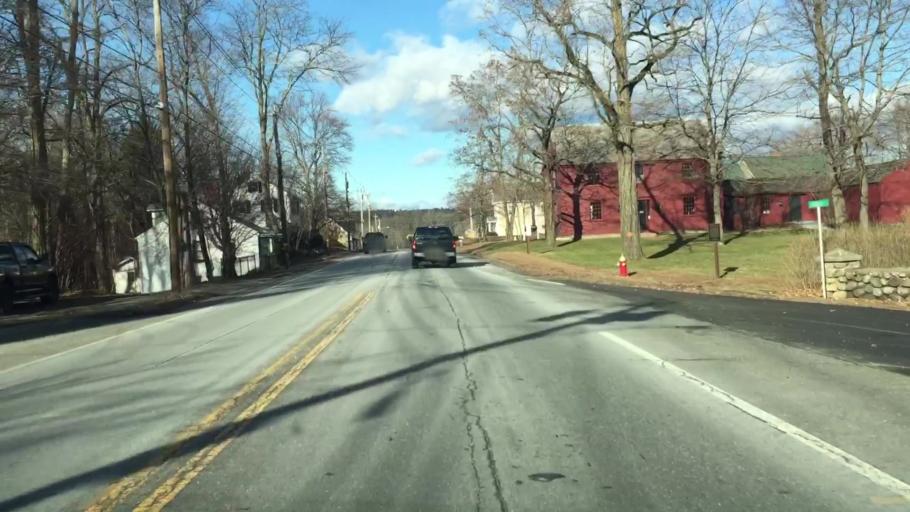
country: US
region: Massachusetts
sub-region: Worcester County
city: West Boylston
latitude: 42.3647
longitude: -71.7815
